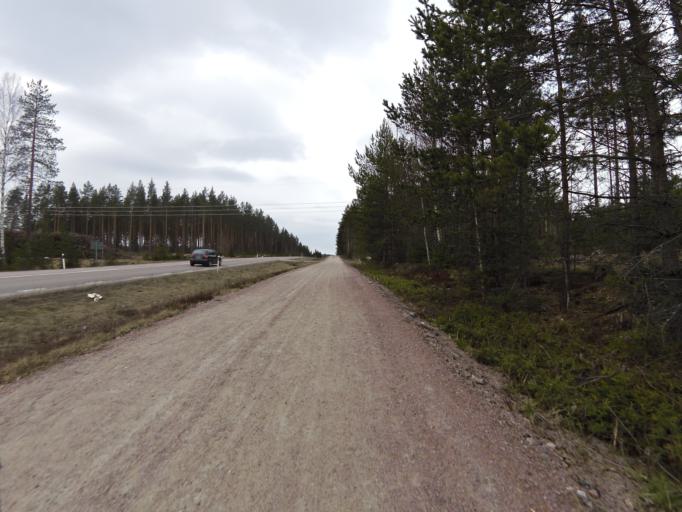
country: SE
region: Gaevleborg
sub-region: Hofors Kommun
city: Hofors
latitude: 60.5418
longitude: 16.2593
